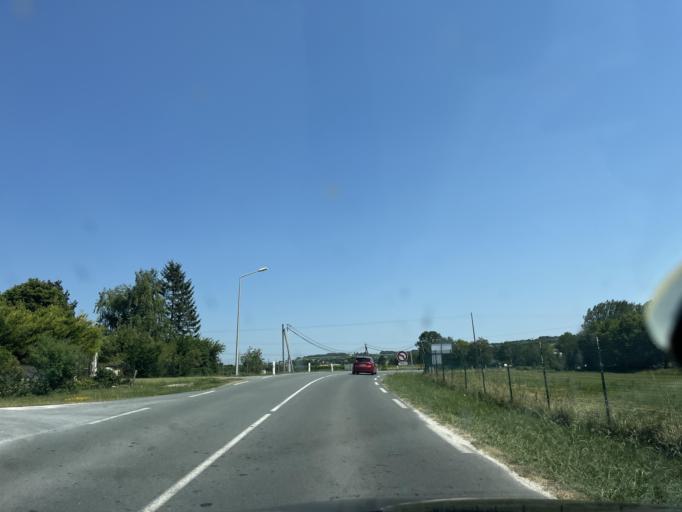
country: FR
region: Poitou-Charentes
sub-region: Departement de la Charente-Maritime
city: Mirambeau
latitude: 45.4212
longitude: -0.6356
